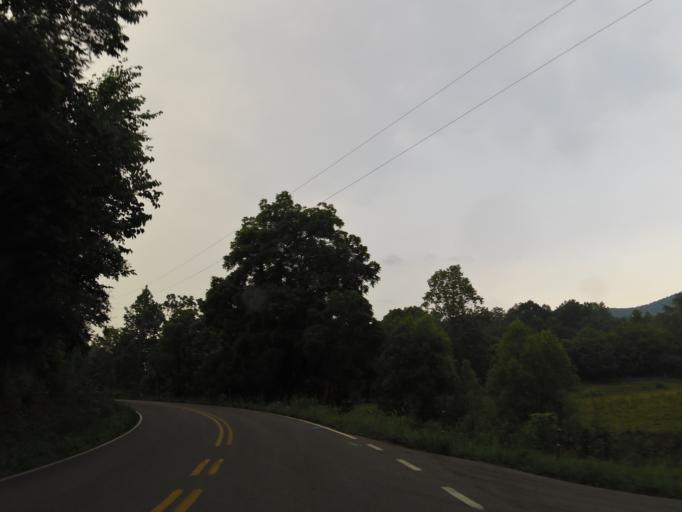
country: US
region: Tennessee
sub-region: Sevier County
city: Seymour
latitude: 35.7991
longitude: -83.7402
